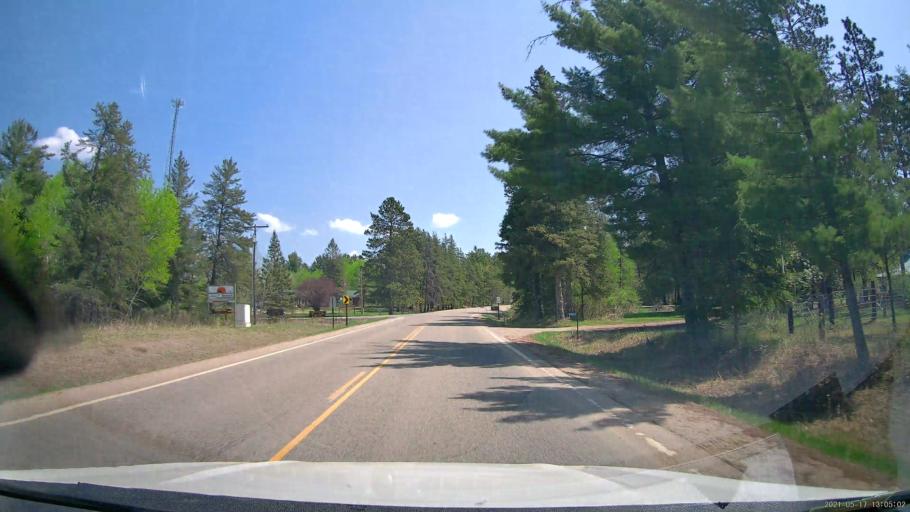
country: US
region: Minnesota
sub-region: Hubbard County
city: Park Rapids
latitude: 47.0650
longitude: -94.9494
